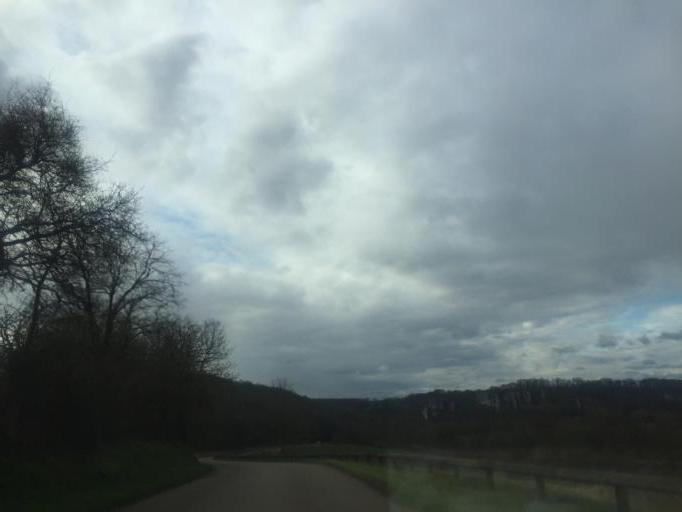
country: FR
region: Bourgogne
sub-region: Departement de la Nievre
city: Clamecy
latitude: 47.4872
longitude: 3.5141
